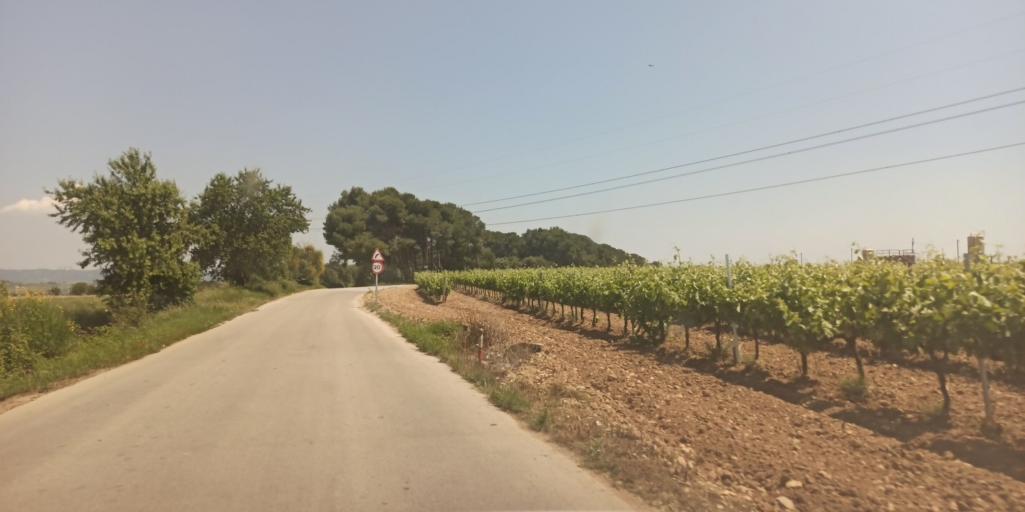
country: ES
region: Catalonia
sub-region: Provincia de Barcelona
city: Sant Marti Sarroca
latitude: 41.3791
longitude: 1.6314
